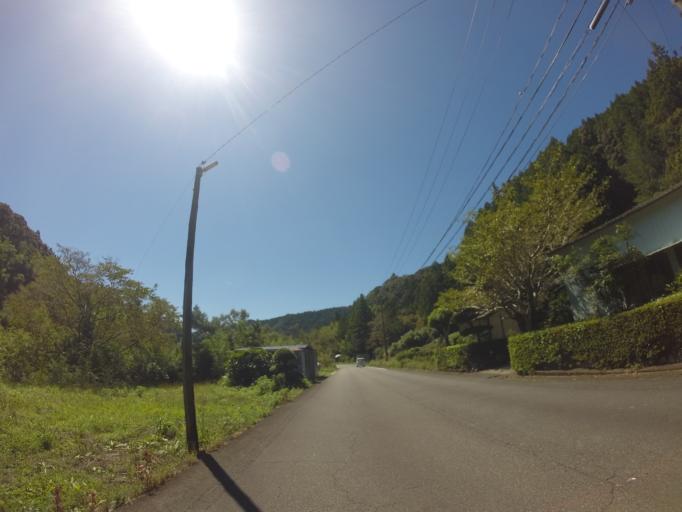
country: JP
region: Shizuoka
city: Fujieda
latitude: 34.9602
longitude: 138.2109
